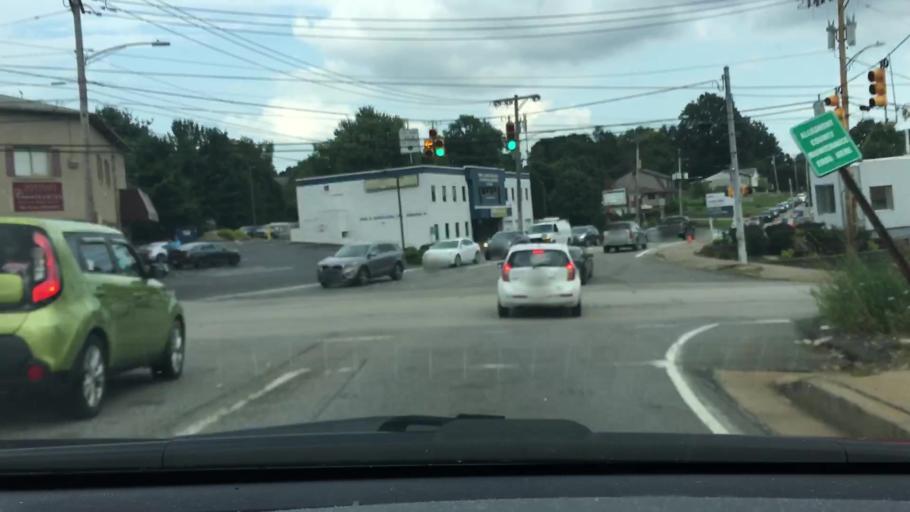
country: US
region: Pennsylvania
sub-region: Allegheny County
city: Castle Shannon
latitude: 40.3452
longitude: -80.0276
